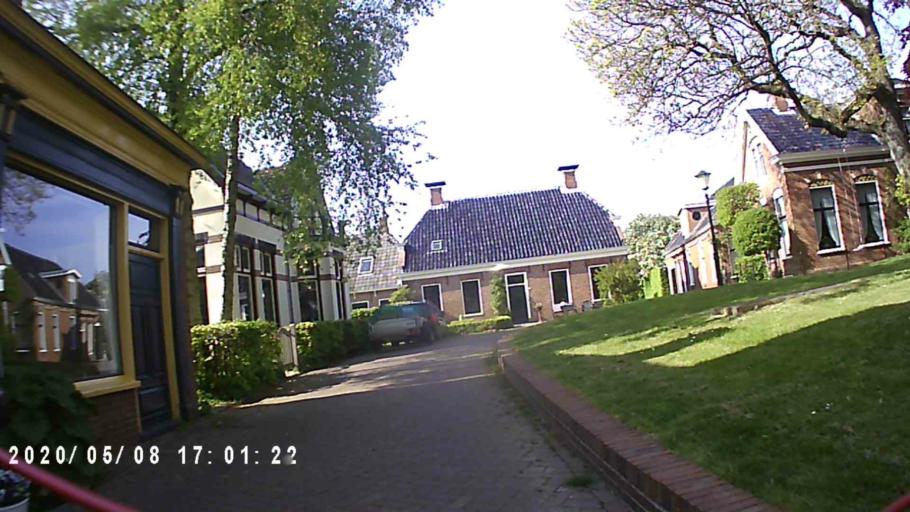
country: NL
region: Groningen
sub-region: Gemeente Bedum
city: Bedum
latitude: 53.4027
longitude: 6.6114
